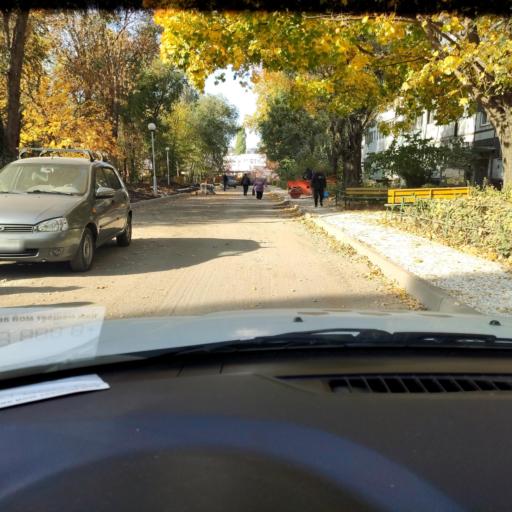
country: RU
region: Samara
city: Tol'yatti
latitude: 53.5185
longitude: 49.2654
